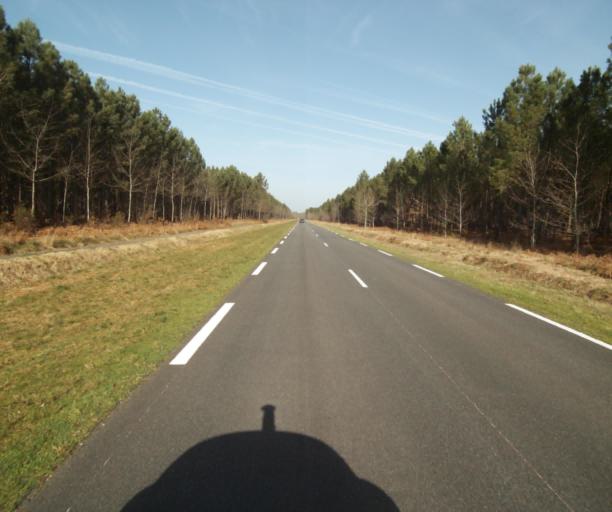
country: FR
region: Aquitaine
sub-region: Departement de la Gironde
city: Grignols
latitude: 44.1885
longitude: -0.1100
